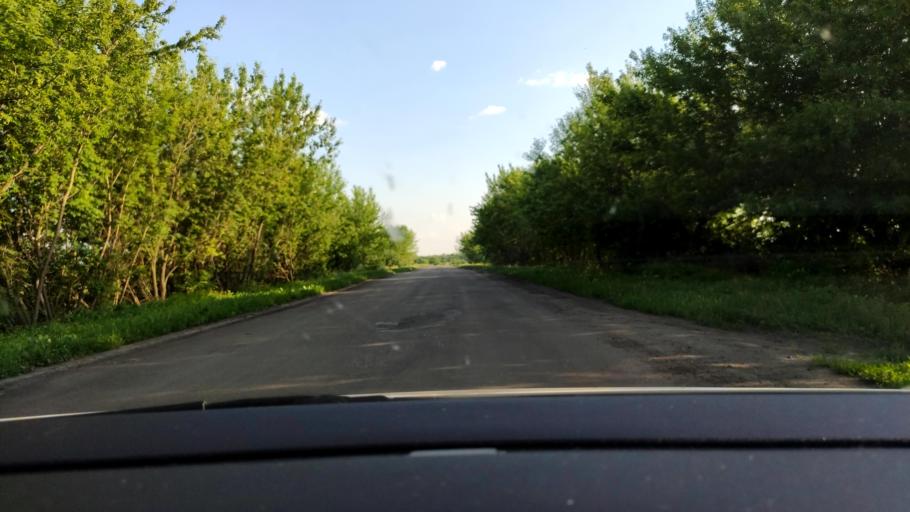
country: RU
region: Voronezj
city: Kashirskoye
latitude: 51.5215
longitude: 39.8348
